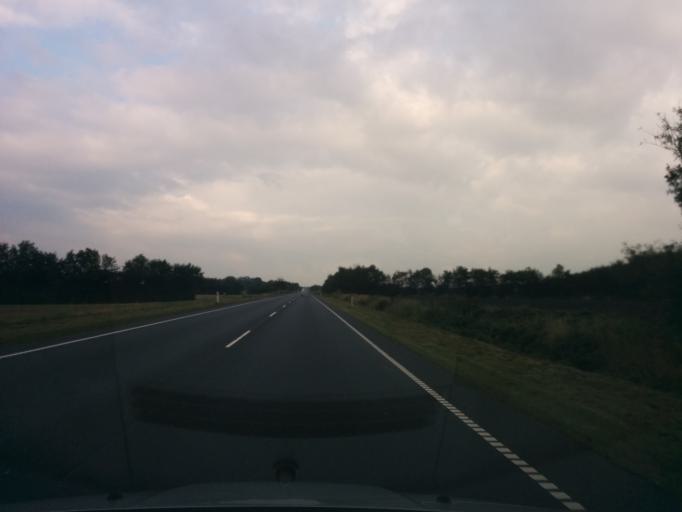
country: DK
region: South Denmark
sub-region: Esbjerg Kommune
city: Bramming
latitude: 55.6097
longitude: 8.7429
